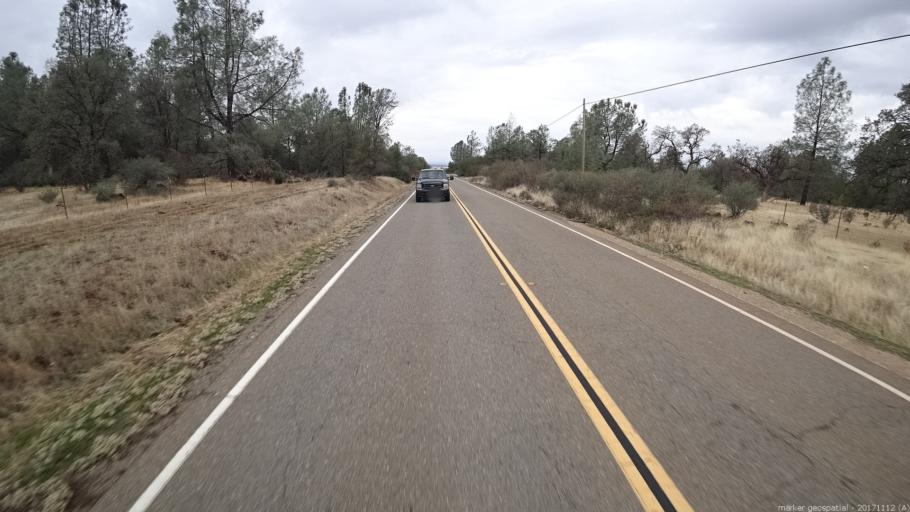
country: US
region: California
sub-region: Shasta County
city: Palo Cedro
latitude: 40.4811
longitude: -122.0867
